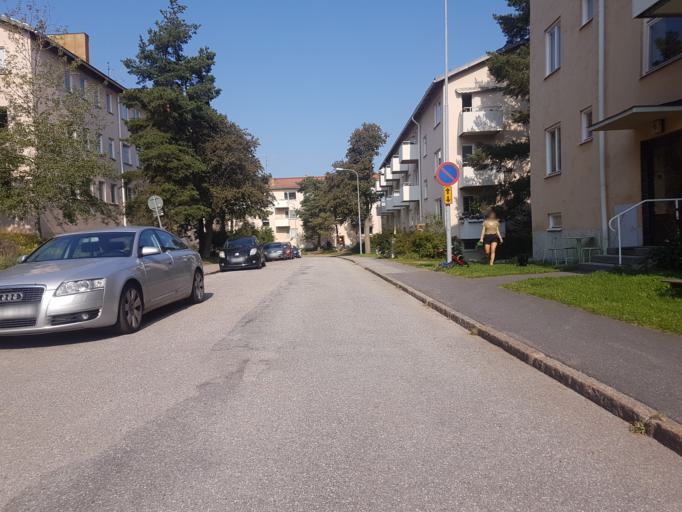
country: SE
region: Stockholm
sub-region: Nacka Kommun
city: Nacka
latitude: 59.2963
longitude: 18.1143
